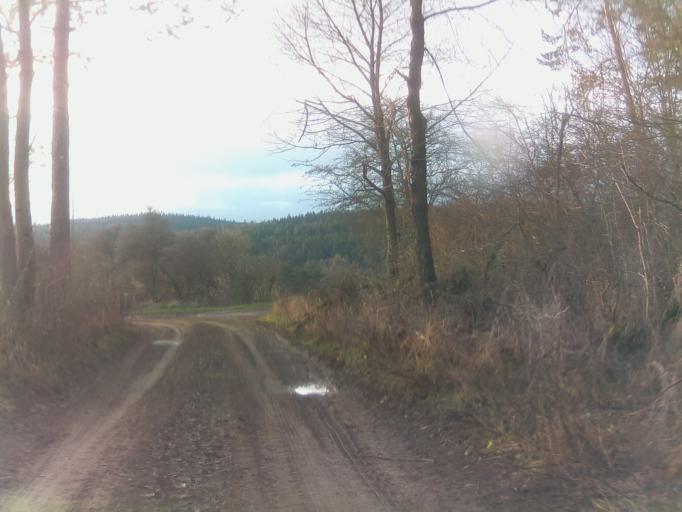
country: DE
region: Thuringia
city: Bad Blankenburg
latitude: 50.7266
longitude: 11.2394
